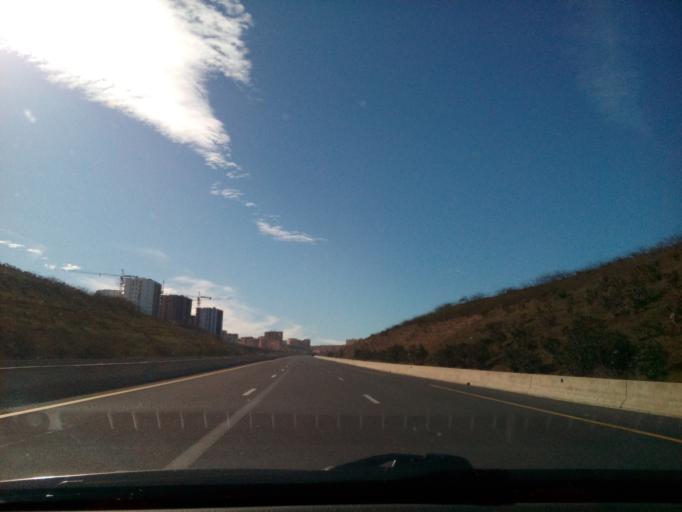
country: DZ
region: Tlemcen
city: Hennaya
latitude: 34.9319
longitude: -1.3422
